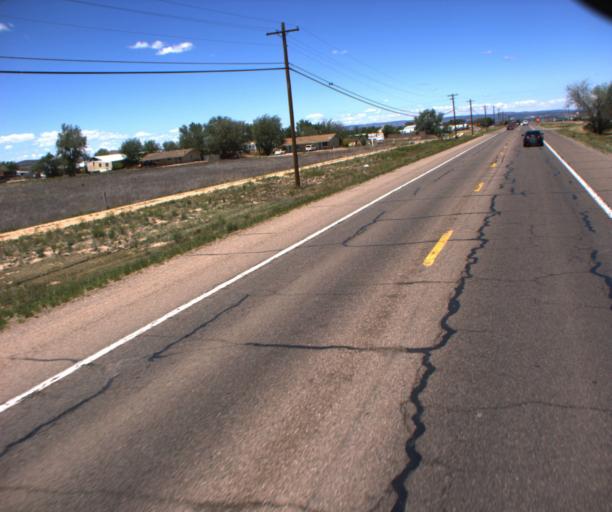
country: US
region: Arizona
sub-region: Yavapai County
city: Chino Valley
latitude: 34.7806
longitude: -112.4525
